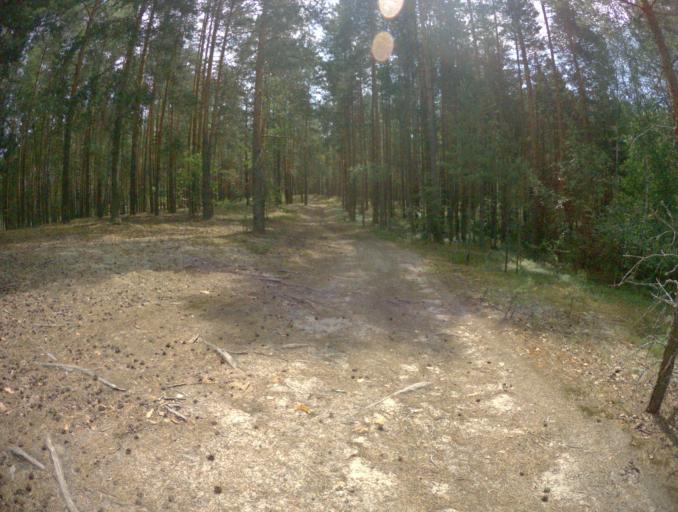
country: RU
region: Ivanovo
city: Talitsy
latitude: 56.3909
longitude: 42.3441
